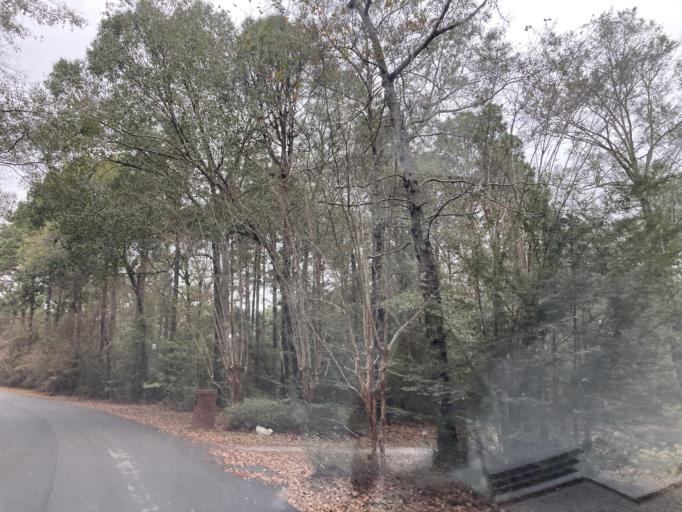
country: US
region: Mississippi
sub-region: Lamar County
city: Purvis
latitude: 31.1559
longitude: -89.4224
